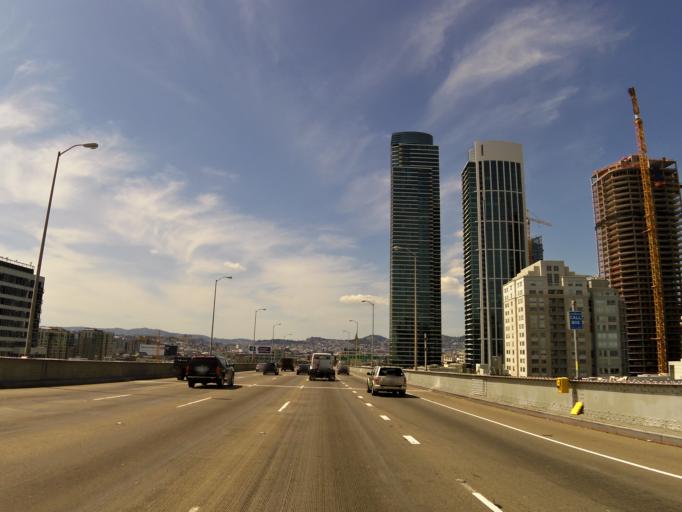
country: US
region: California
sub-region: San Francisco County
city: San Francisco
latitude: 37.7878
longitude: -122.3890
